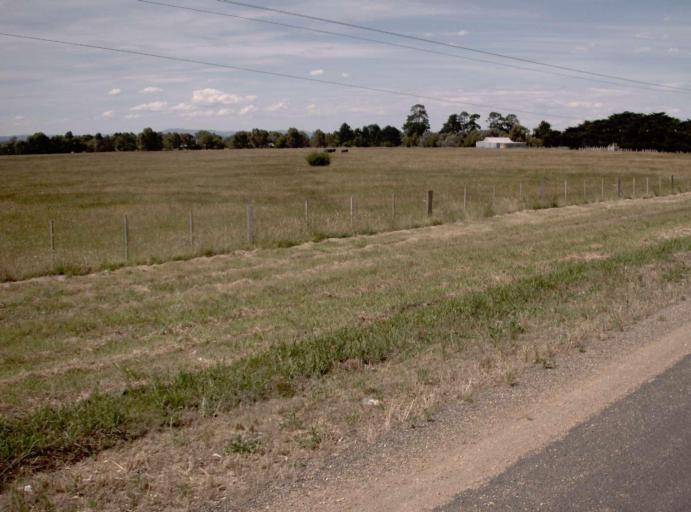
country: AU
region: Victoria
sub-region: East Gippsland
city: Bairnsdale
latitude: -37.8467
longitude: 147.5694
